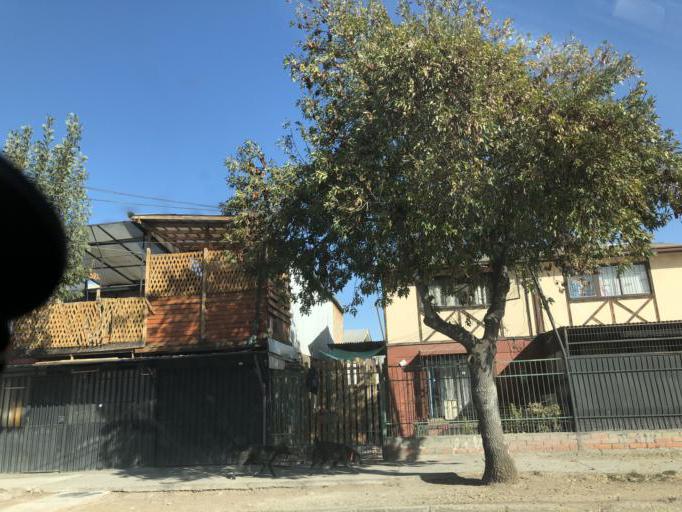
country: CL
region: Santiago Metropolitan
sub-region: Provincia de Cordillera
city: Puente Alto
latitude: -33.6214
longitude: -70.5924
